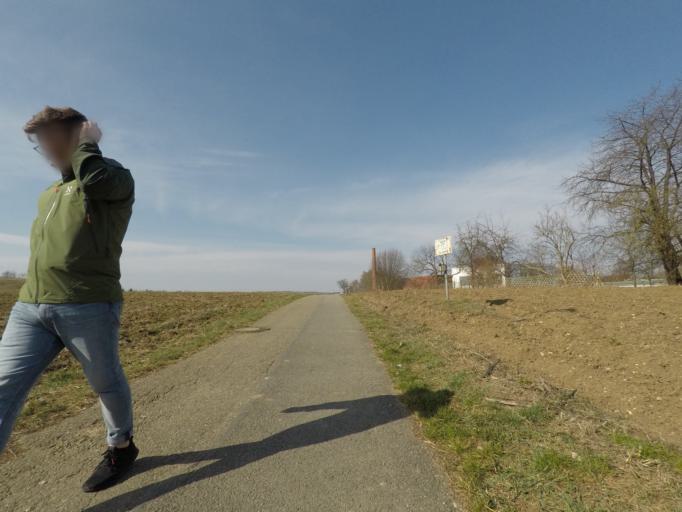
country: DE
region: Baden-Wuerttemberg
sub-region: Tuebingen Region
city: Metzingen
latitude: 48.5293
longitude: 9.3006
